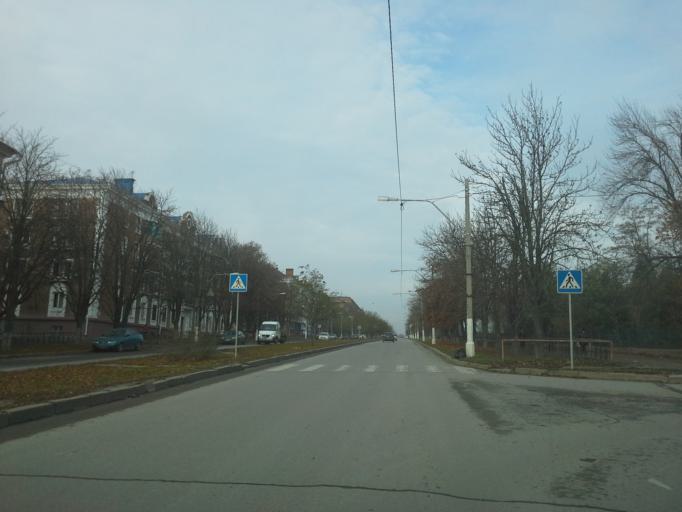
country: RU
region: Volgograd
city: Vodstroy
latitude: 48.7788
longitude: 44.5729
